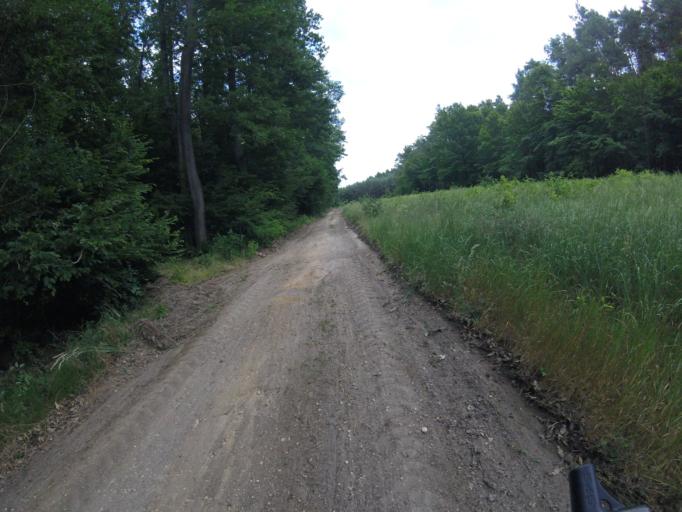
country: HU
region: Zala
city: Turje
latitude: 47.0368
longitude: 17.0658
